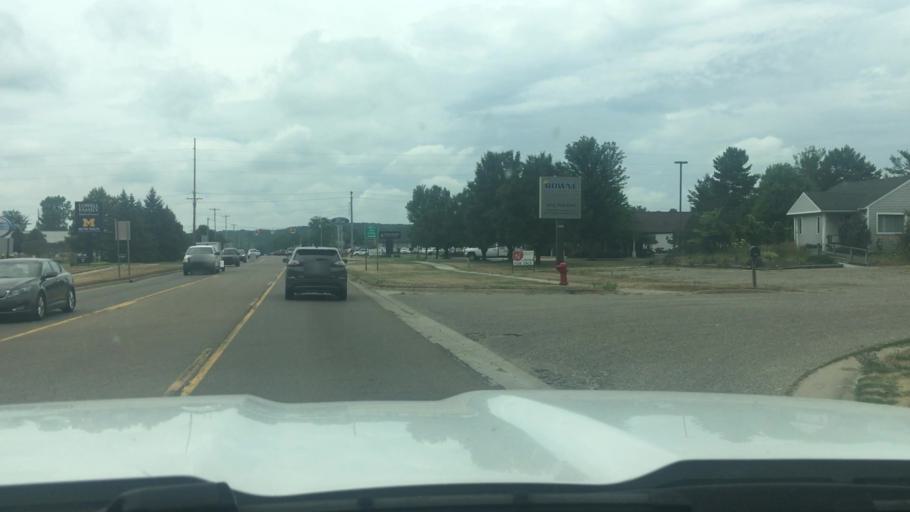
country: US
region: Michigan
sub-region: Kent County
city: Lowell
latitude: 42.9310
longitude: -85.3689
